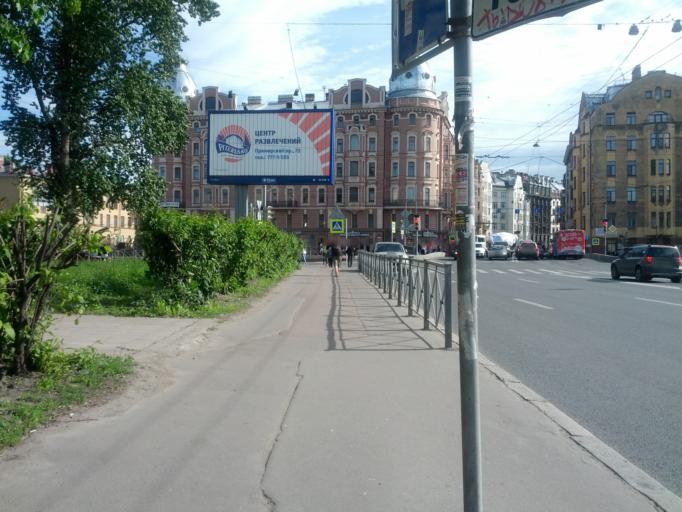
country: RU
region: St.-Petersburg
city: Petrogradka
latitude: 59.9686
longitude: 30.3144
